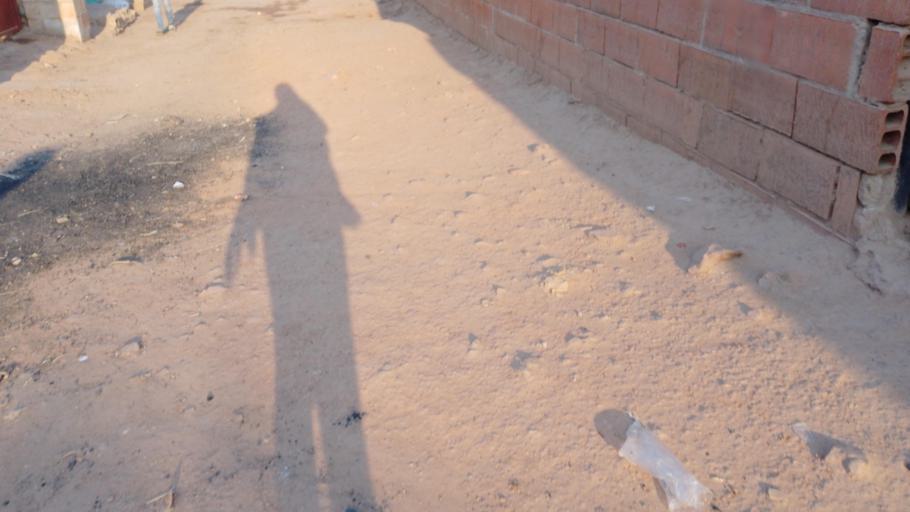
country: ZM
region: Lusaka
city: Lusaka
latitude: -15.3975
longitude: 28.3729
